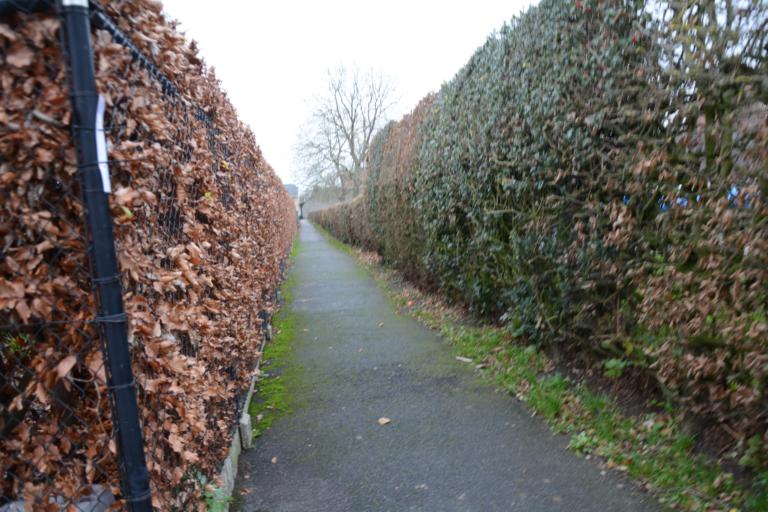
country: BE
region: Flanders
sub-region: Provincie Vlaams-Brabant
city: Opwijk
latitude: 50.9426
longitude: 4.1673
